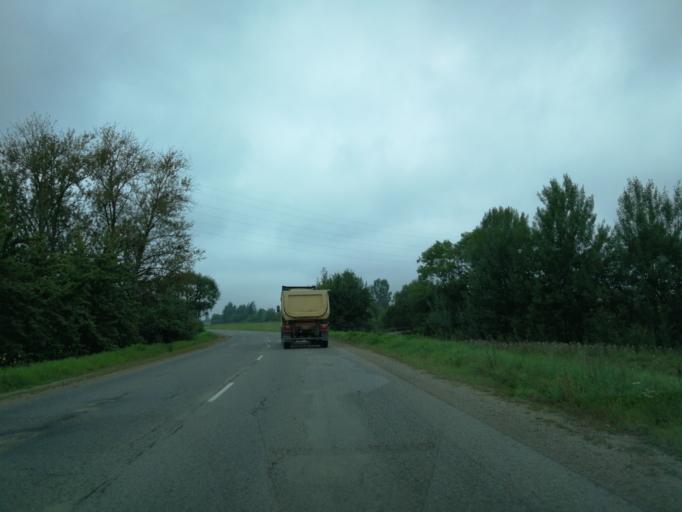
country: LV
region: Jekabpils Rajons
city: Jekabpils
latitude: 56.5013
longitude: 25.8989
